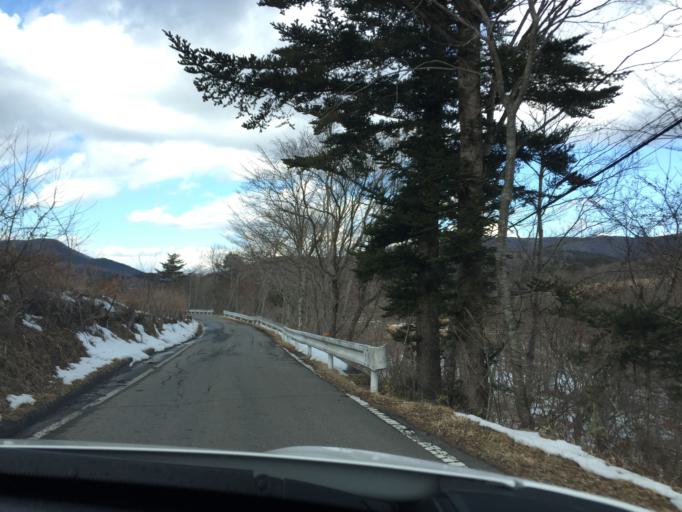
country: JP
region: Fukushima
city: Funehikimachi-funehiki
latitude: 37.2882
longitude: 140.7187
